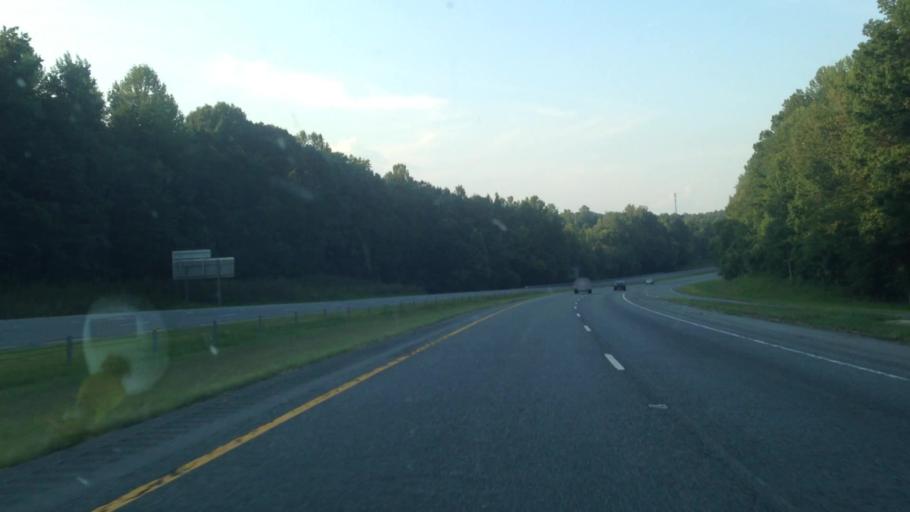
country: US
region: North Carolina
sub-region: Rockingham County
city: Reidsville
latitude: 36.4044
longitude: -79.5968
